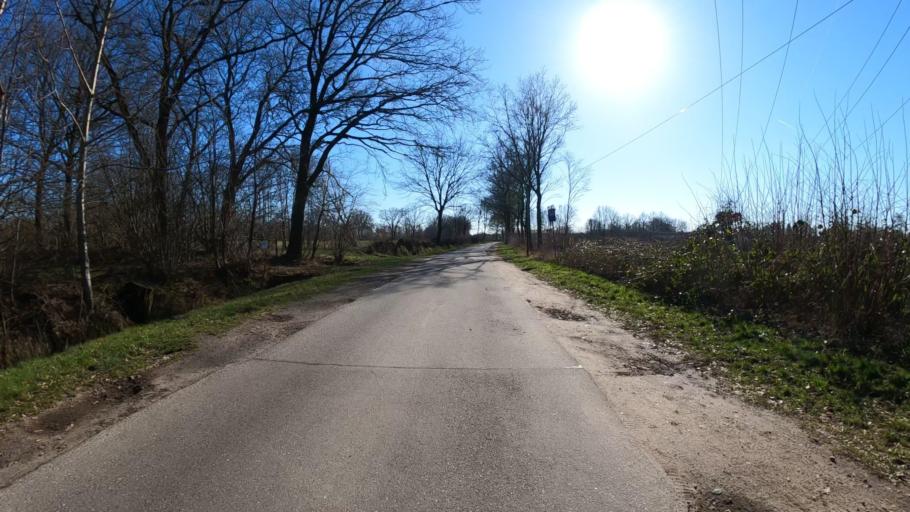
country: DE
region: Schleswig-Holstein
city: Kummerfeld
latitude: 53.6828
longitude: 9.7847
